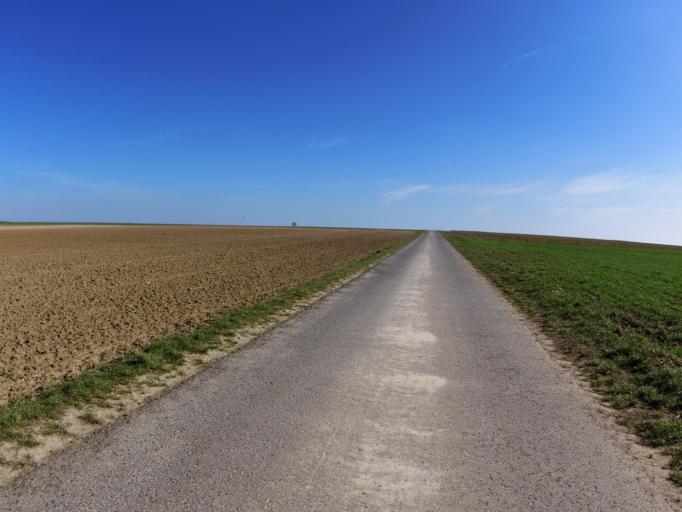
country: DE
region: Bavaria
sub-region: Regierungsbezirk Unterfranken
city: Prosselsheim
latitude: 49.8560
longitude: 10.1128
